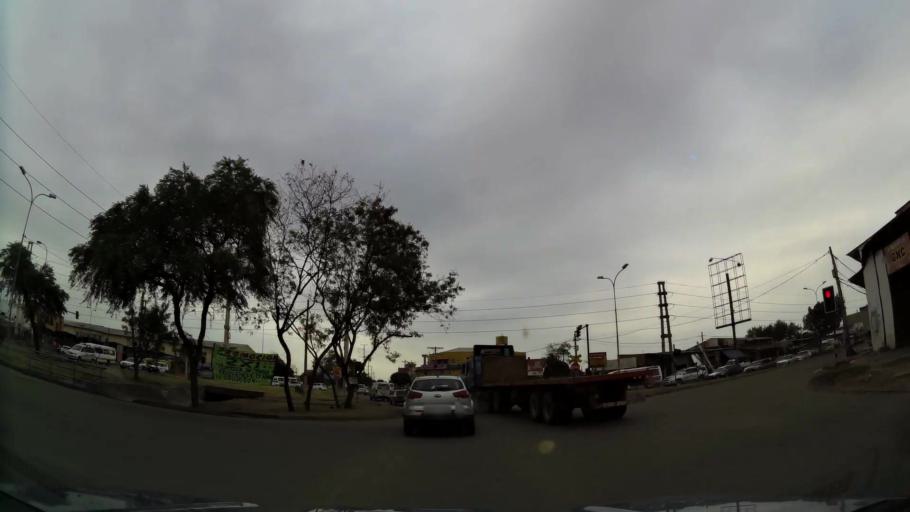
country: BO
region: Santa Cruz
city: Santa Cruz de la Sierra
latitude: -17.7898
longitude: -63.1481
